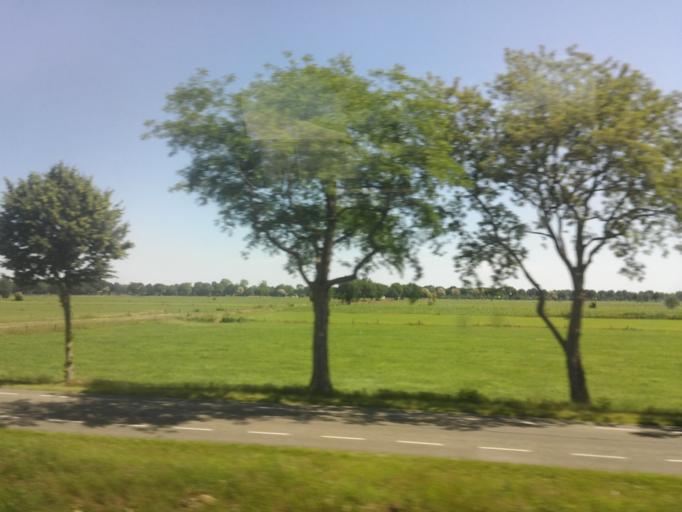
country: NL
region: Overijssel
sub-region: Gemeente Staphorst
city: Staphorst
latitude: 52.6420
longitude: 6.2237
